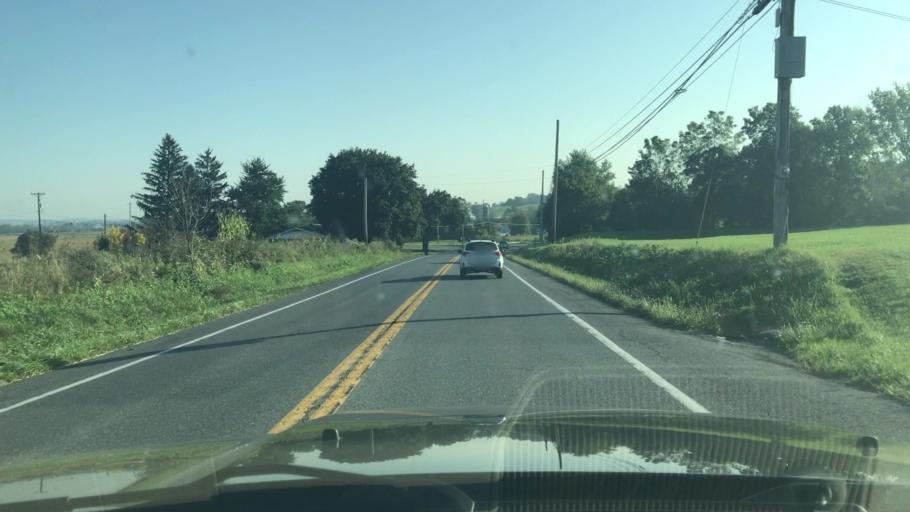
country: US
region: Pennsylvania
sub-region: Berks County
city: Topton
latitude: 40.4875
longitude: -75.7290
